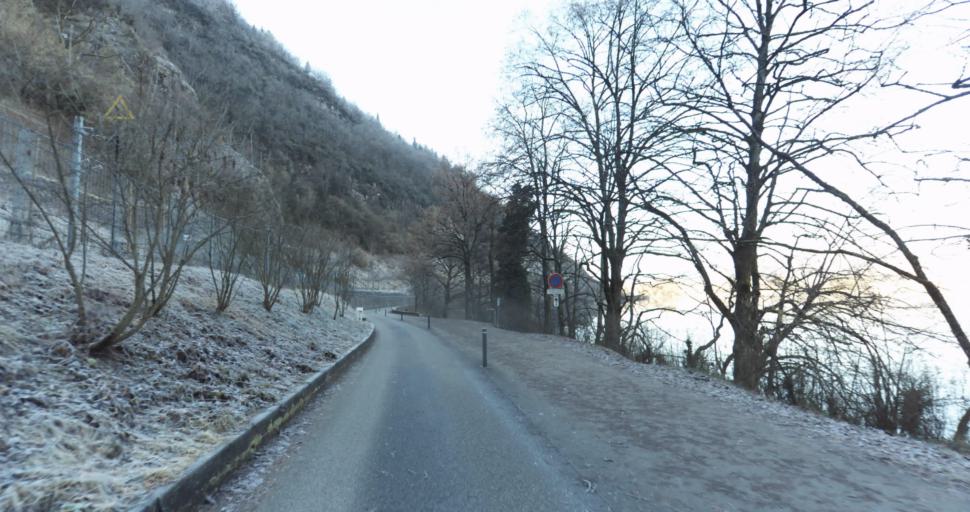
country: FR
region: Rhone-Alpes
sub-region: Departement de l'Ain
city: Montreal-la-Cluse
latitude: 46.1603
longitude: 5.5809
